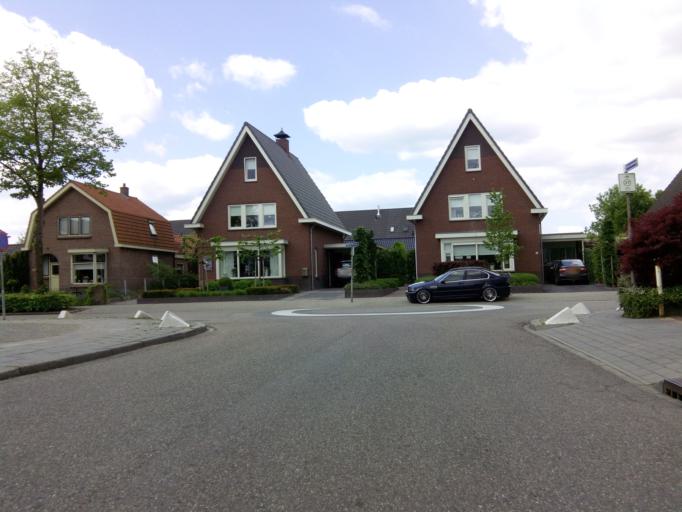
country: NL
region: Gelderland
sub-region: Gemeente Ede
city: Ederveen
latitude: 52.0607
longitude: 5.5776
